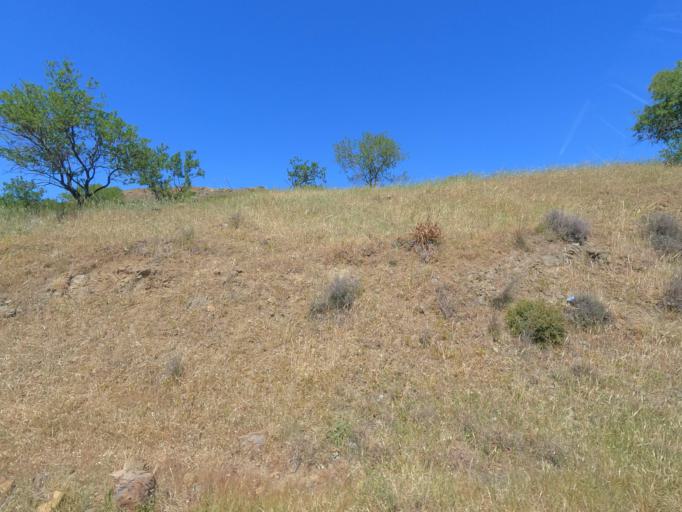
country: CY
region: Lefkosia
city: Peristerona
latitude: 35.0594
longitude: 33.0733
